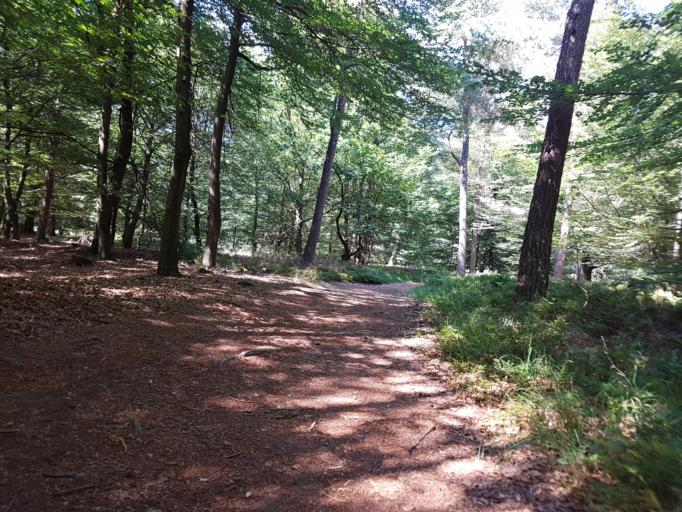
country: NL
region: North Brabant
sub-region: Gemeente Haaren
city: Haaren
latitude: 51.5824
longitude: 5.2567
